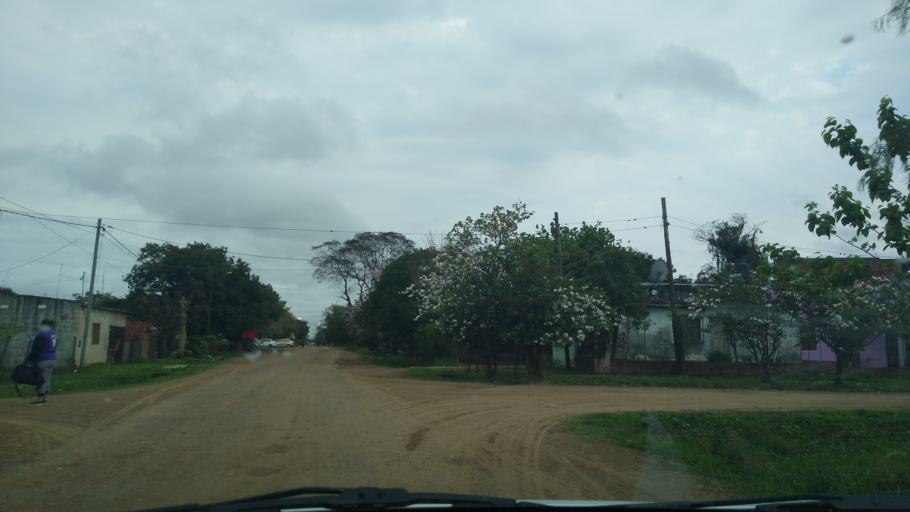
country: AR
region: Chaco
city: Barranqueras
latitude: -27.4765
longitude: -58.9187
